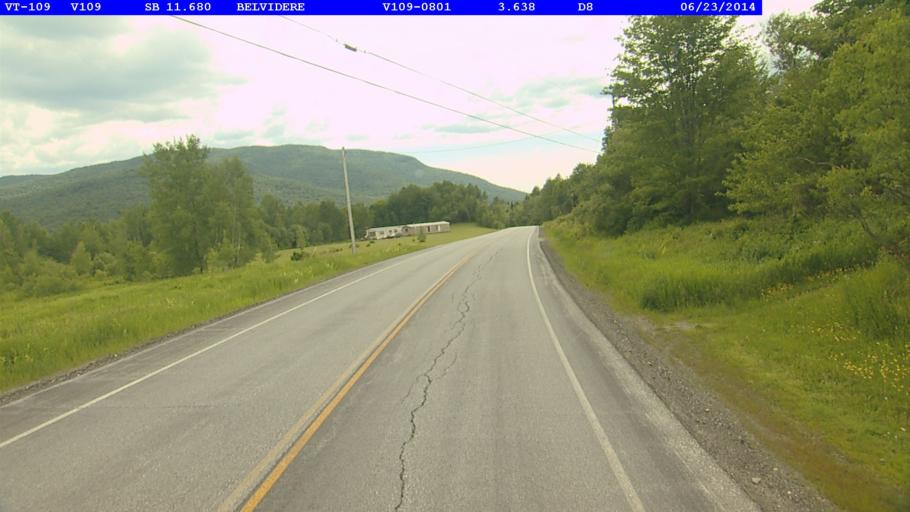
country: US
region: Vermont
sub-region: Lamoille County
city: Johnson
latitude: 44.7568
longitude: -72.6802
